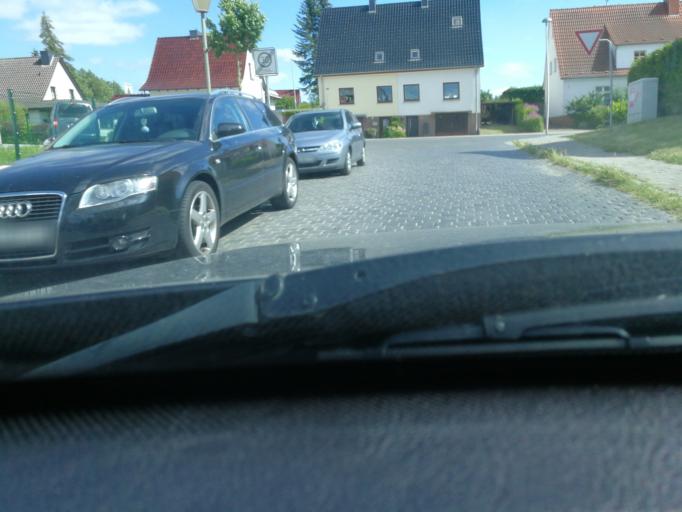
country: DE
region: Mecklenburg-Vorpommern
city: Stralsund
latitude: 54.3030
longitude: 13.0679
